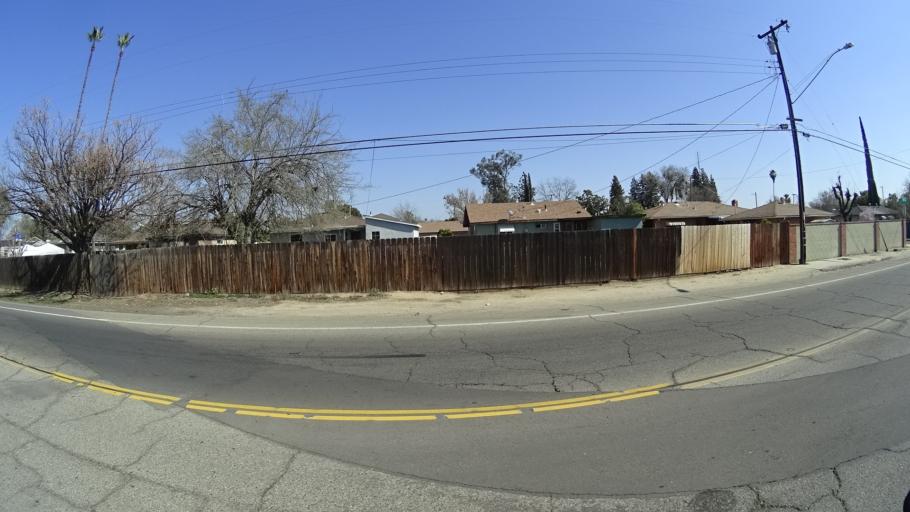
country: US
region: California
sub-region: Fresno County
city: Fresno
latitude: 36.7609
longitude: -119.8248
